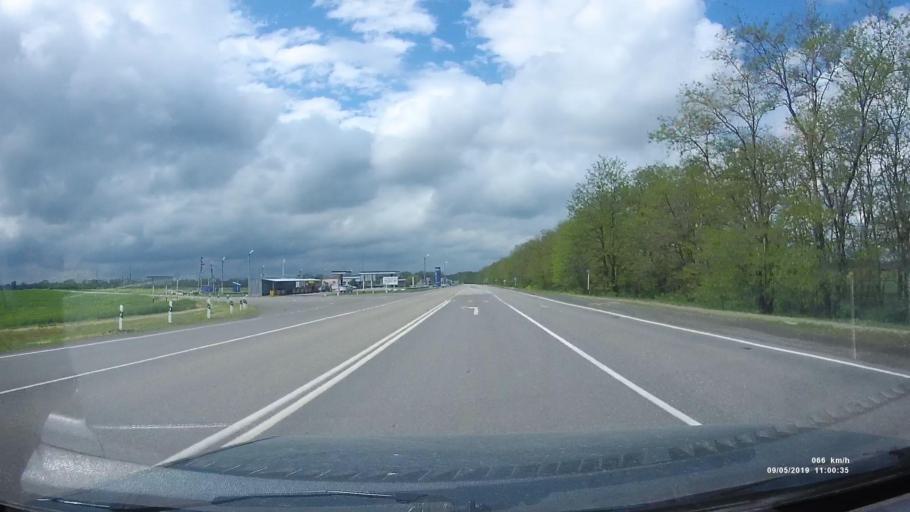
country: RU
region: Rostov
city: Peshkovo
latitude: 46.8527
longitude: 39.2173
